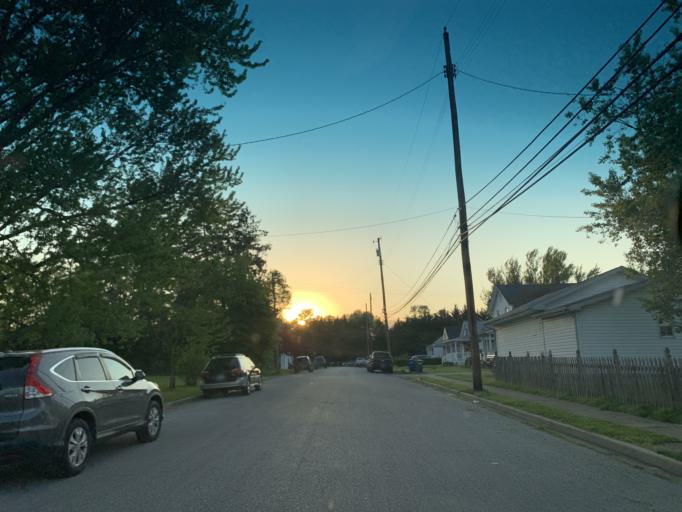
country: US
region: Maryland
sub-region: Harford County
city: Aberdeen
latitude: 39.5099
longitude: -76.1693
